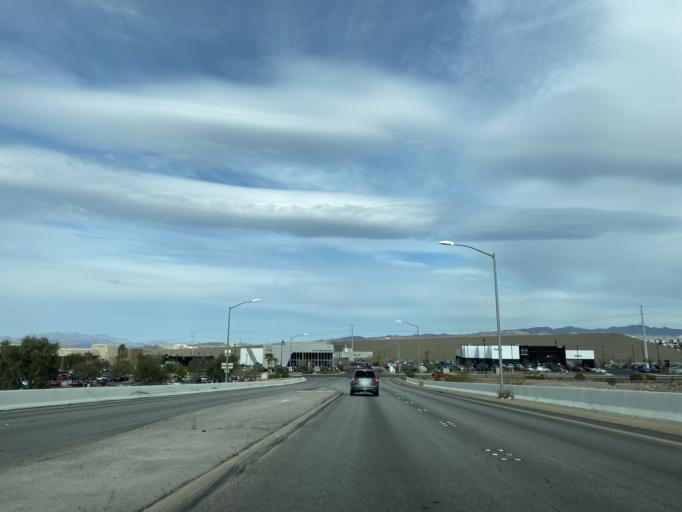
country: US
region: Nevada
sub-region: Clark County
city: Henderson
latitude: 36.0463
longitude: -115.0211
